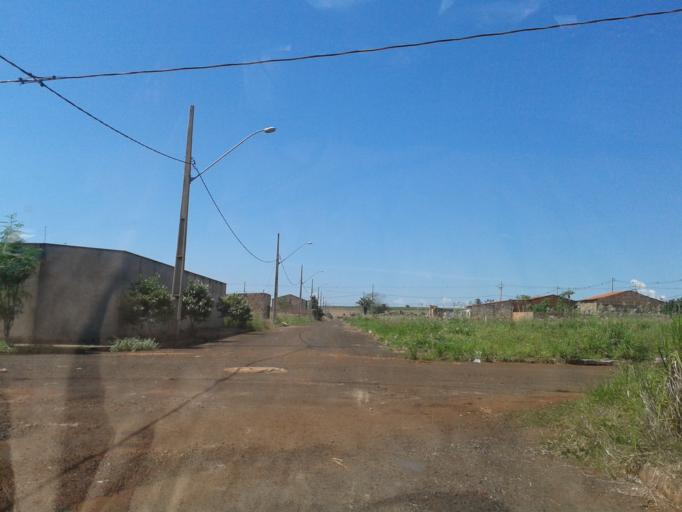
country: BR
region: Goias
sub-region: Itumbiara
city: Itumbiara
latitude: -18.4218
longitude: -49.1851
